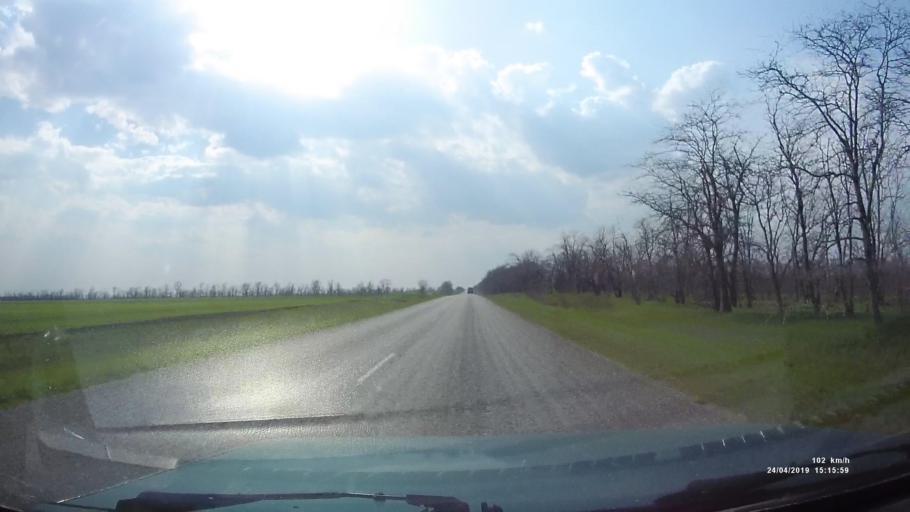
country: RU
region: Rostov
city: Remontnoye
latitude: 46.5465
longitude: 43.2230
